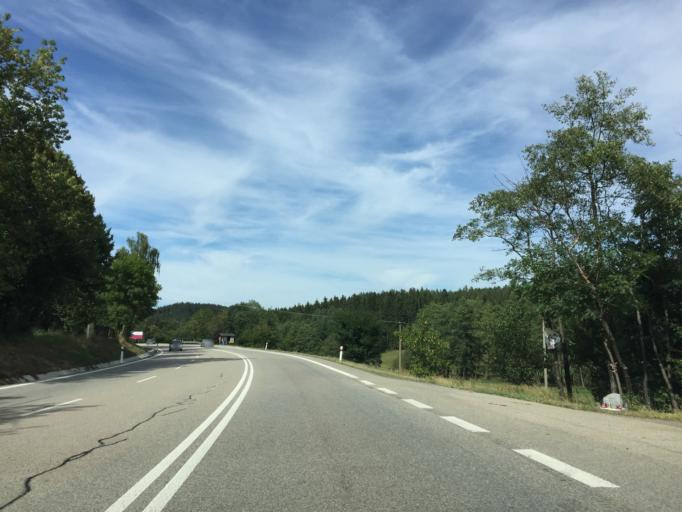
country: CZ
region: Central Bohemia
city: Votice
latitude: 49.6119
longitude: 14.6610
